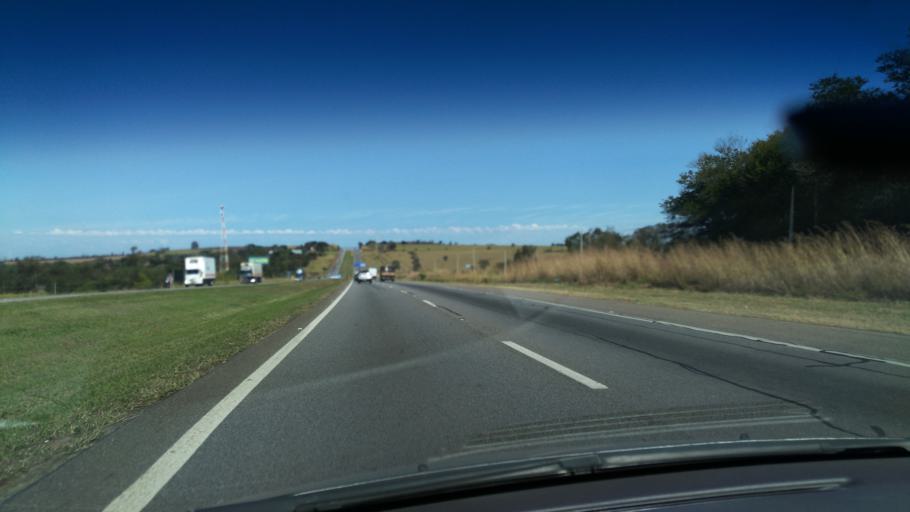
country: BR
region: Sao Paulo
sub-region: Jaguariuna
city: Jaguariuna
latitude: -22.7455
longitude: -47.0200
